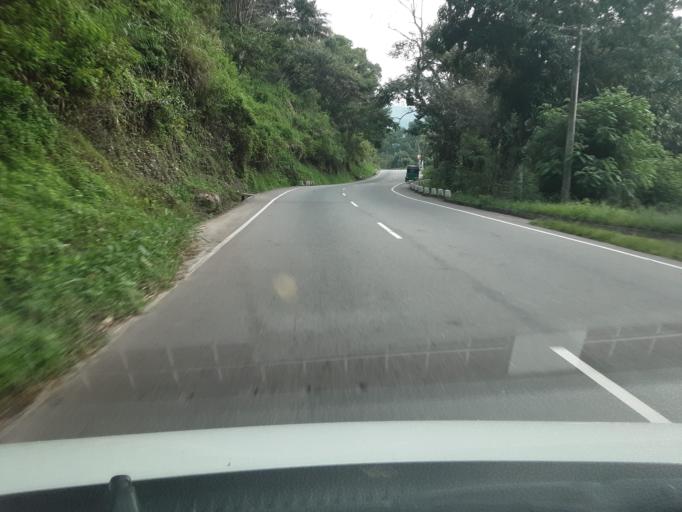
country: LK
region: Uva
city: Badulla
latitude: 6.9440
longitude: 81.0171
